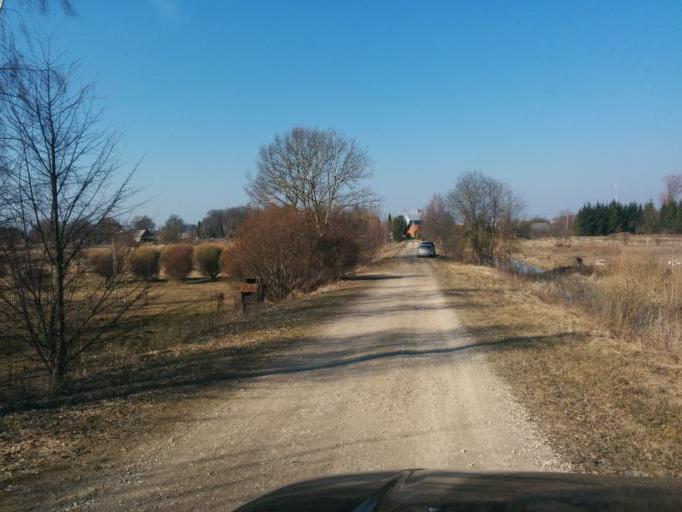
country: LV
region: Ozolnieku
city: Ozolnieki
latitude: 56.6403
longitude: 23.7762
